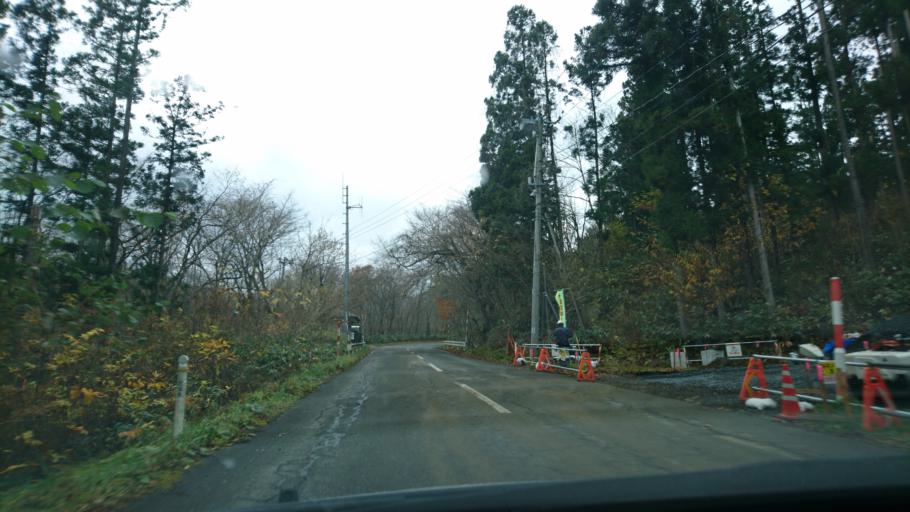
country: JP
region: Iwate
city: Ichinoseki
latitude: 38.9129
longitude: 140.8765
